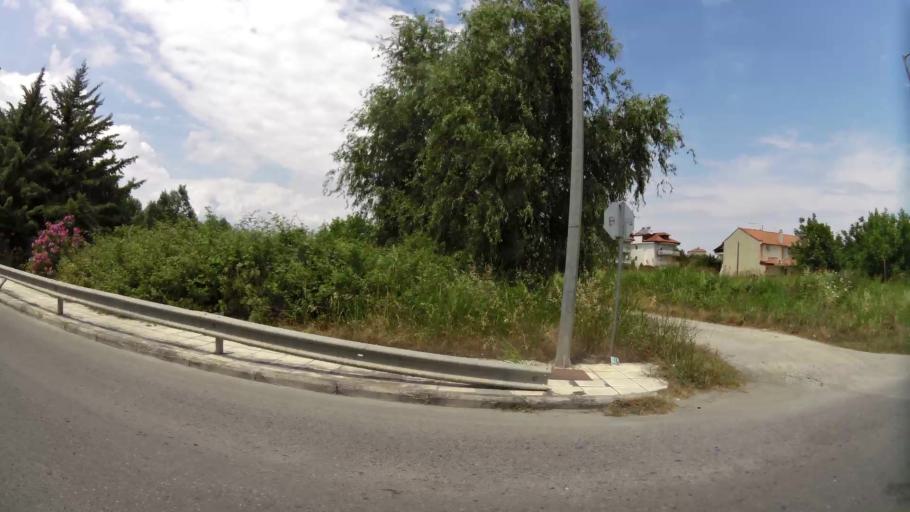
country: GR
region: Central Macedonia
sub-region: Nomos Pierias
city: Peristasi
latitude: 40.2634
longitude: 22.5338
